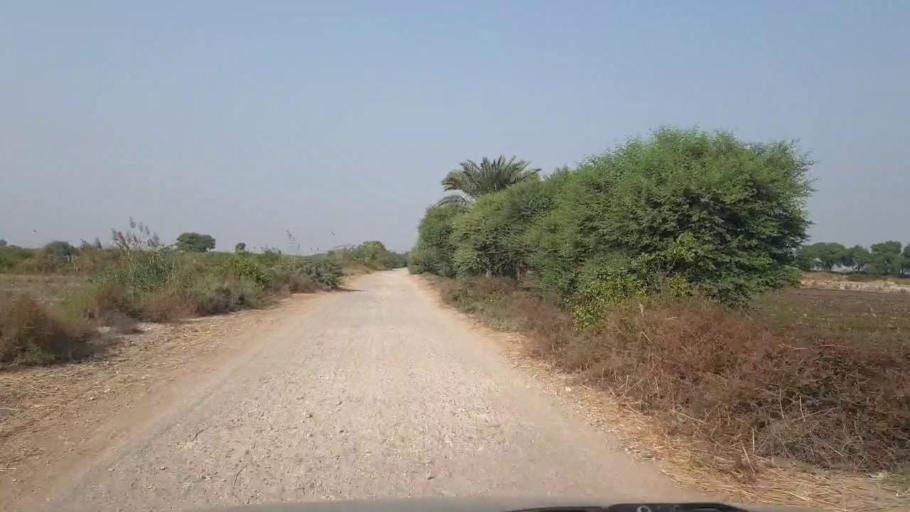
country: PK
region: Sindh
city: Tando Muhammad Khan
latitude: 25.0919
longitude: 68.3387
